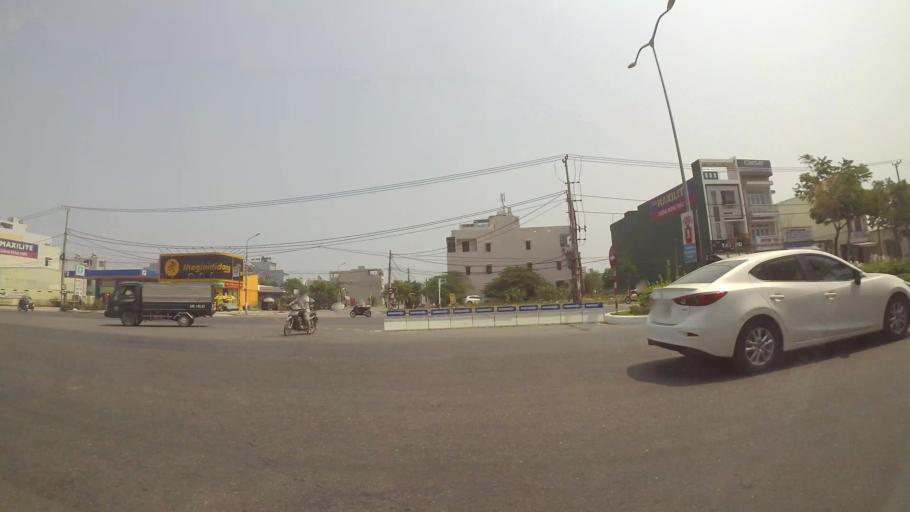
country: VN
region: Da Nang
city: Ngu Hanh Son
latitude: 16.0128
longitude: 108.2557
